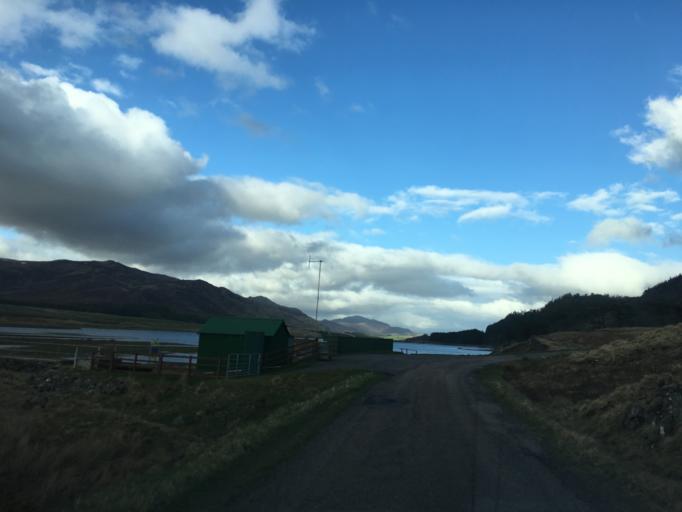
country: GB
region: Scotland
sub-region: Highland
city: Kingussie
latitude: 57.0056
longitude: -4.3704
